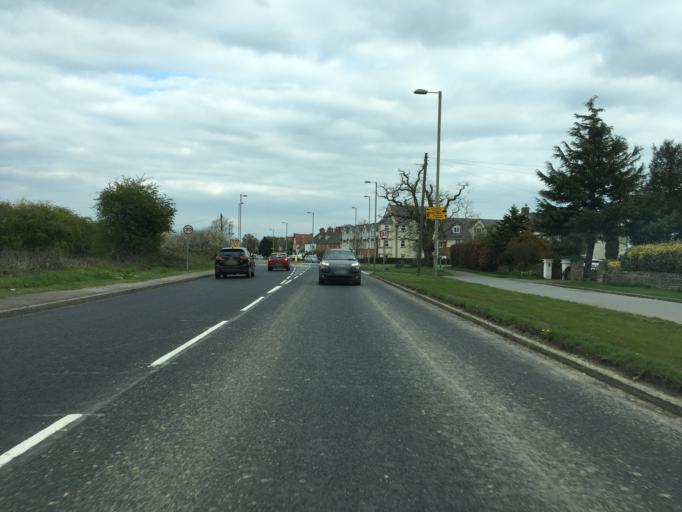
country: GB
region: England
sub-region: Oxfordshire
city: Witney
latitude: 51.7902
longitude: -1.5027
